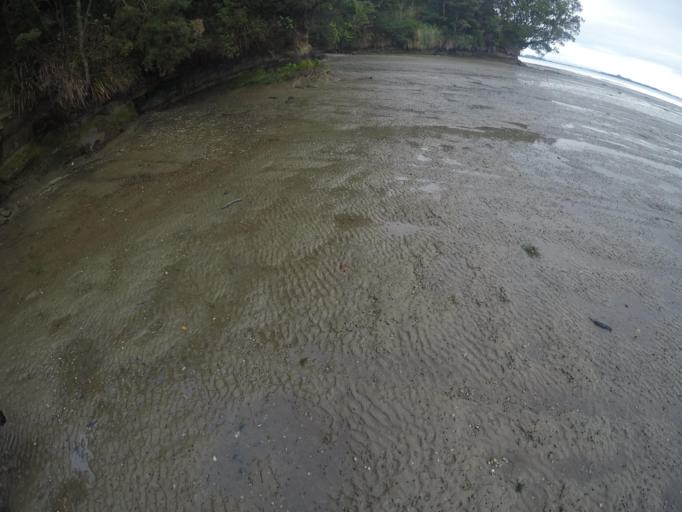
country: NZ
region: Auckland
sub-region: Auckland
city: Titirangi
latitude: -36.9438
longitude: 174.6664
